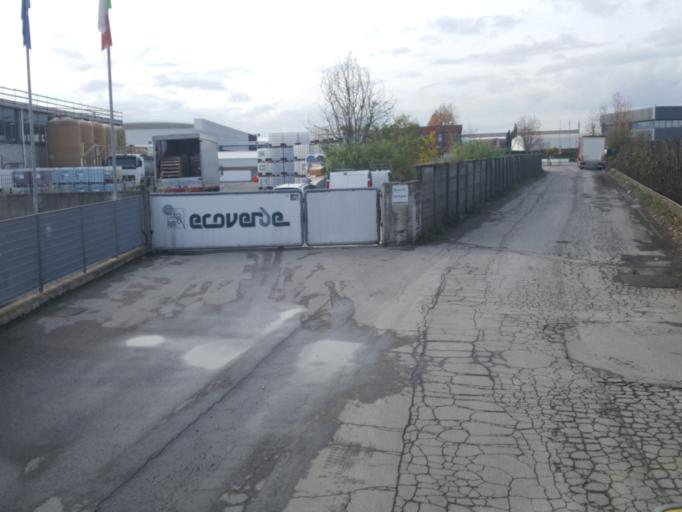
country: IT
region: Tuscany
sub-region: Provincia di Lucca
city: Porcari
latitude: 43.8221
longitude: 10.6150
